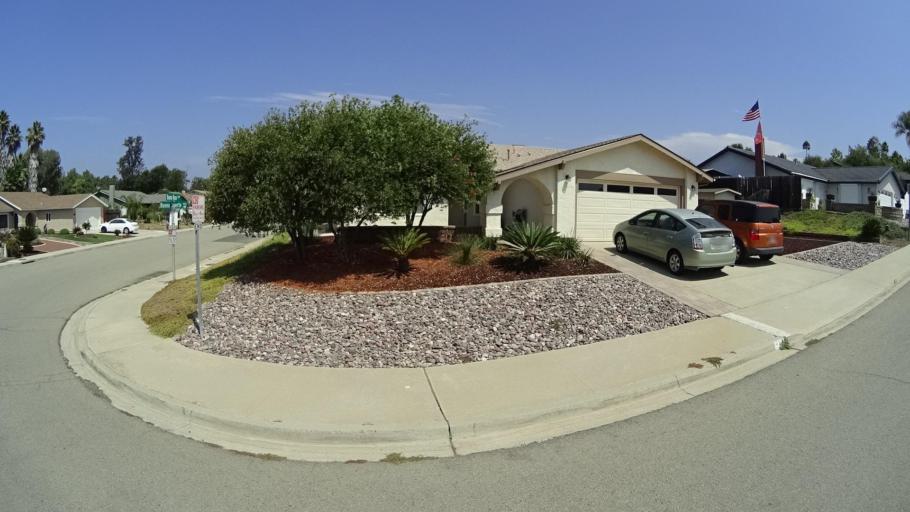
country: US
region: California
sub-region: San Diego County
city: Fallbrook
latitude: 33.3438
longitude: -117.2399
